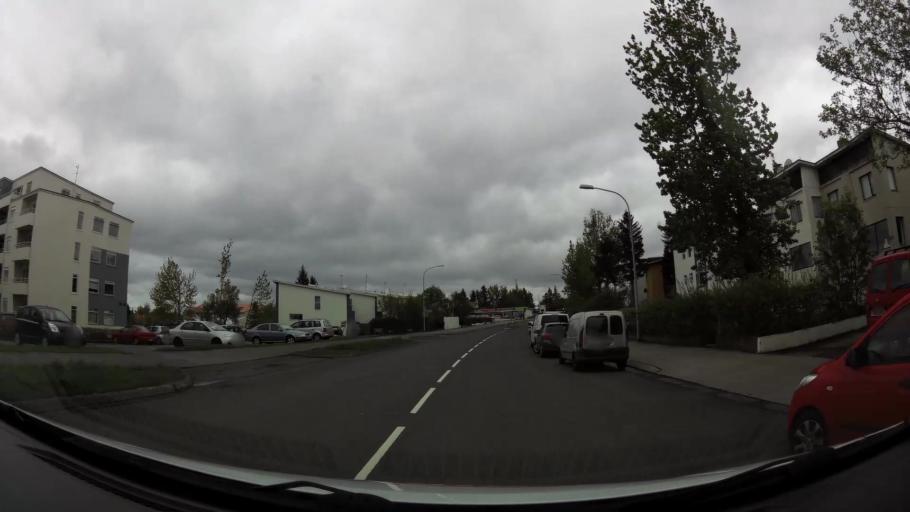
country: IS
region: Capital Region
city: Reykjavik
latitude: 64.1365
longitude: -21.8616
